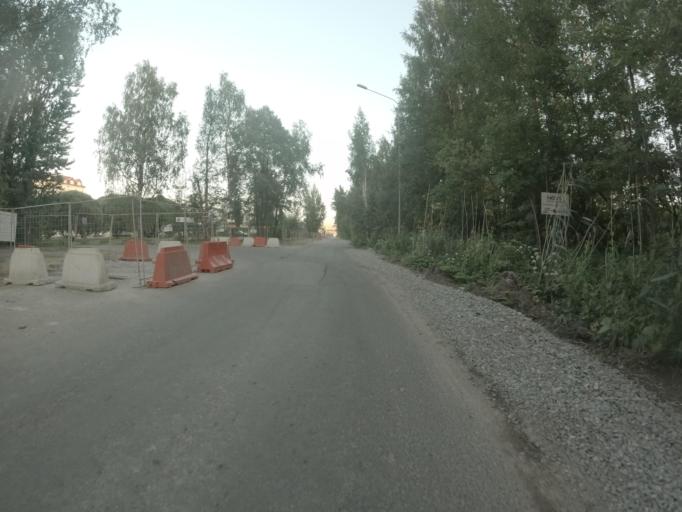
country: RU
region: St.-Petersburg
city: Krasnogvargeisky
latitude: 59.9462
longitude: 30.4480
